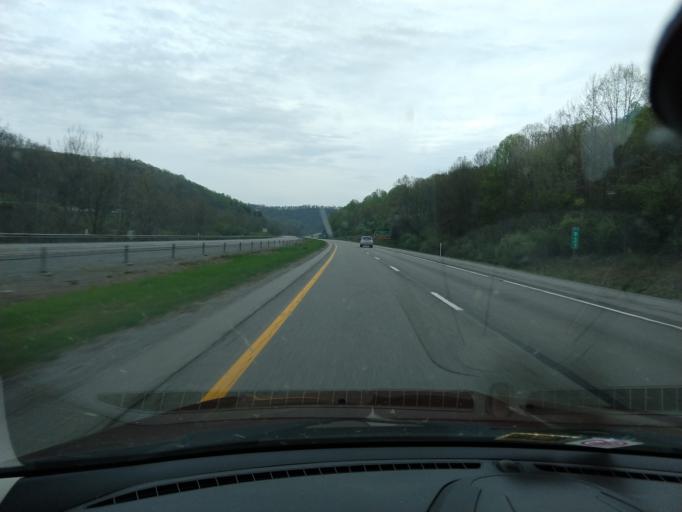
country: US
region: West Virginia
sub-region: Lewis County
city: Weston
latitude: 38.9992
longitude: -80.5019
